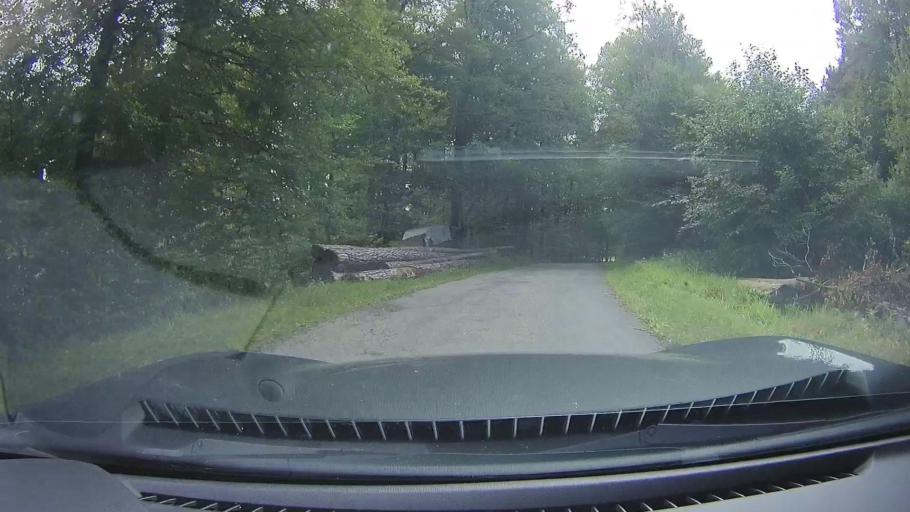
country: DE
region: Baden-Wuerttemberg
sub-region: Regierungsbezirk Stuttgart
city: Spiegelberg
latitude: 49.0388
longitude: 9.4625
